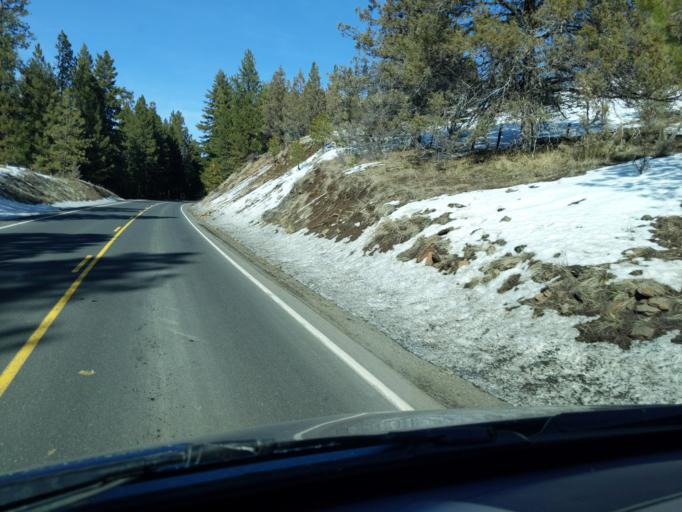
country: US
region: Oregon
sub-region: Grant County
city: John Day
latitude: 44.8836
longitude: -119.0143
